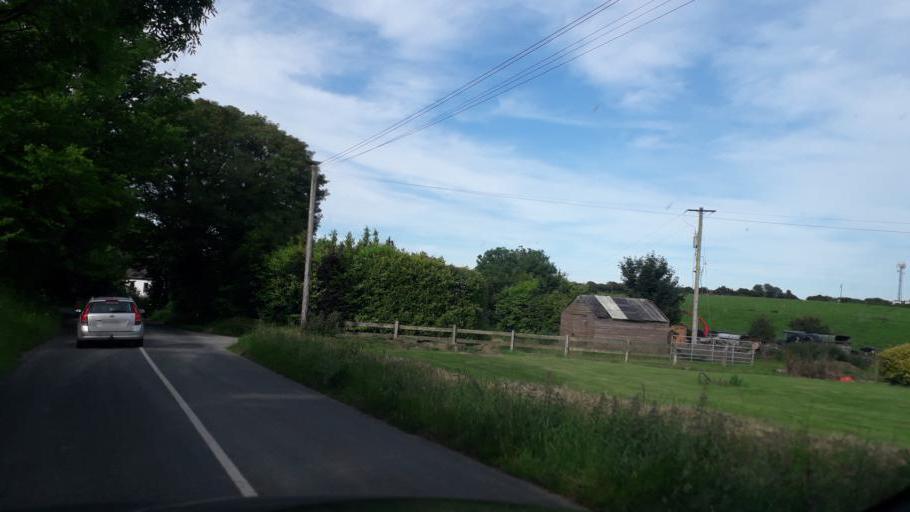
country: IE
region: Leinster
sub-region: Loch Garman
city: Courtown
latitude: 52.5675
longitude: -6.2303
